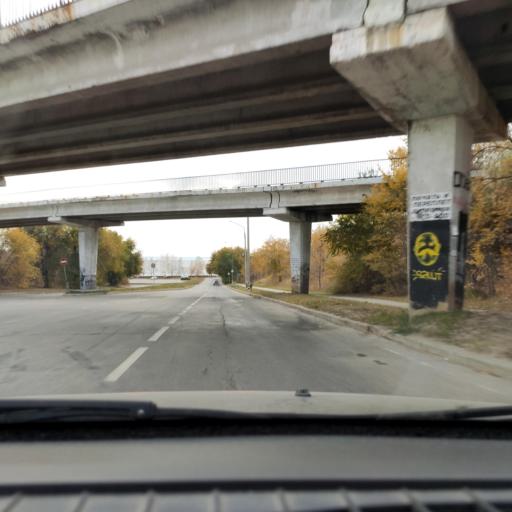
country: RU
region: Samara
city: Tol'yatti
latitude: 53.4976
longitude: 49.2698
